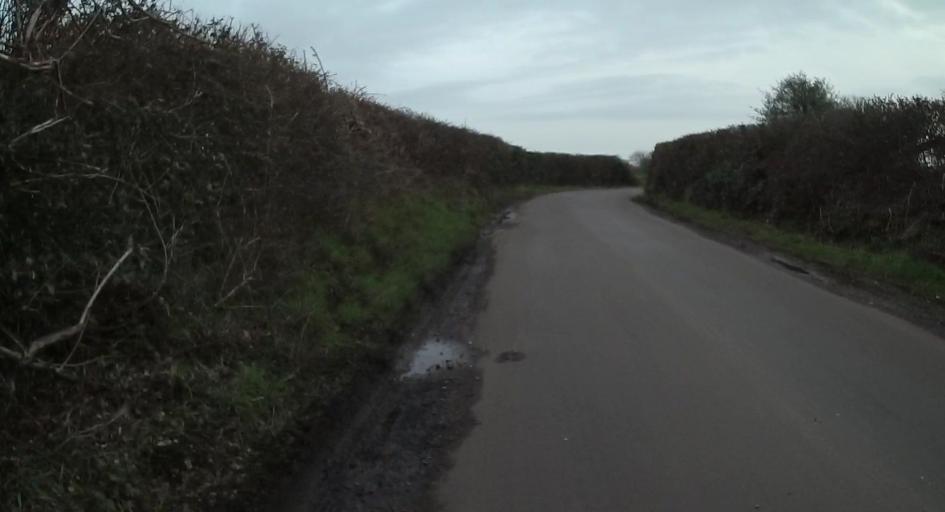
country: GB
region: England
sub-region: West Berkshire
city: Stratfield Mortimer
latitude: 51.3720
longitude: -1.0687
